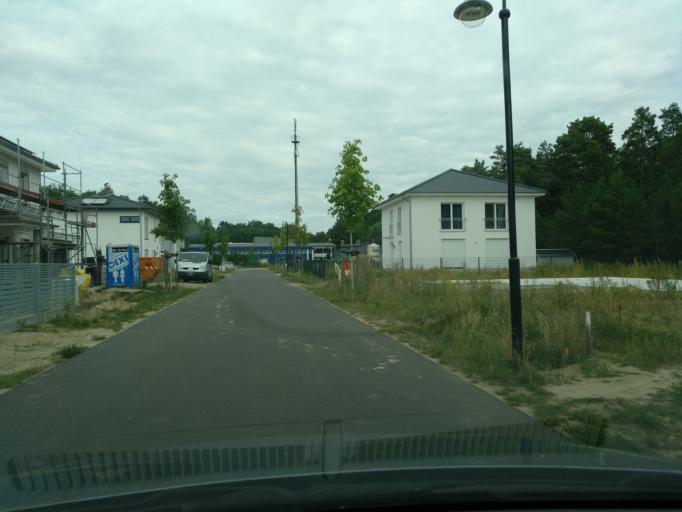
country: DE
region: Brandenburg
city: Bad Saarow
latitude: 52.2784
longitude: 14.0673
